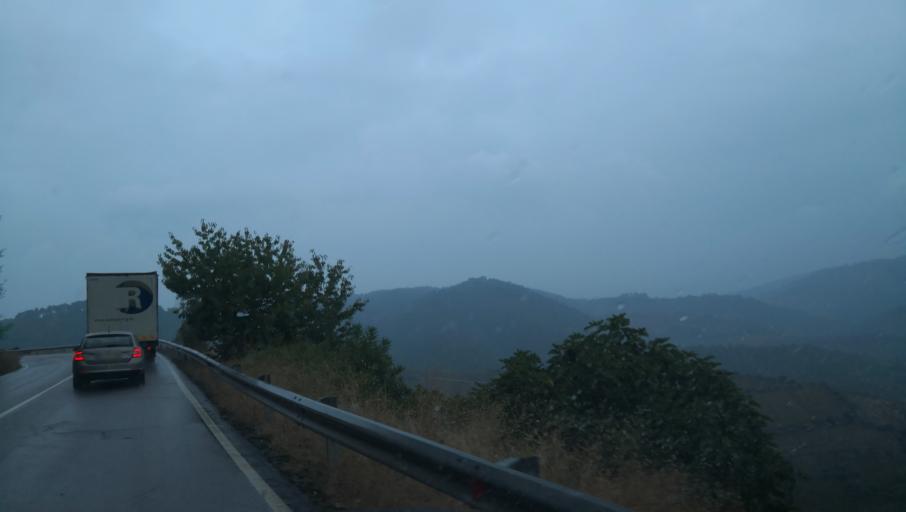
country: PT
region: Vila Real
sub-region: Vila Real
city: Vila Real
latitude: 41.2307
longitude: -7.7273
